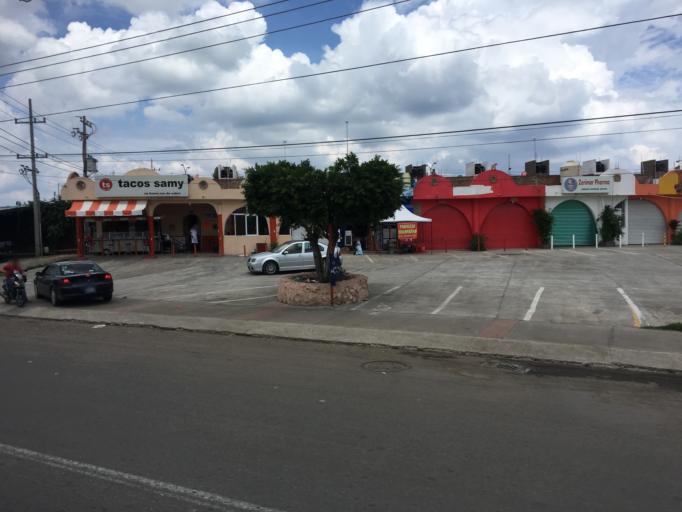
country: MX
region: Guanajuato
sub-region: Irapuato
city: Ex-Hacienda del Copal
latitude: 20.7139
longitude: -101.3503
